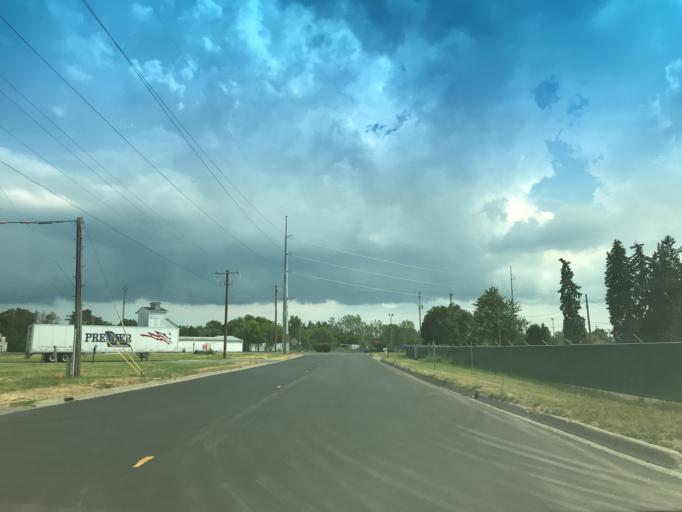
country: US
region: Michigan
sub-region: Eaton County
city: Waverly
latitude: 42.6990
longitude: -84.6313
